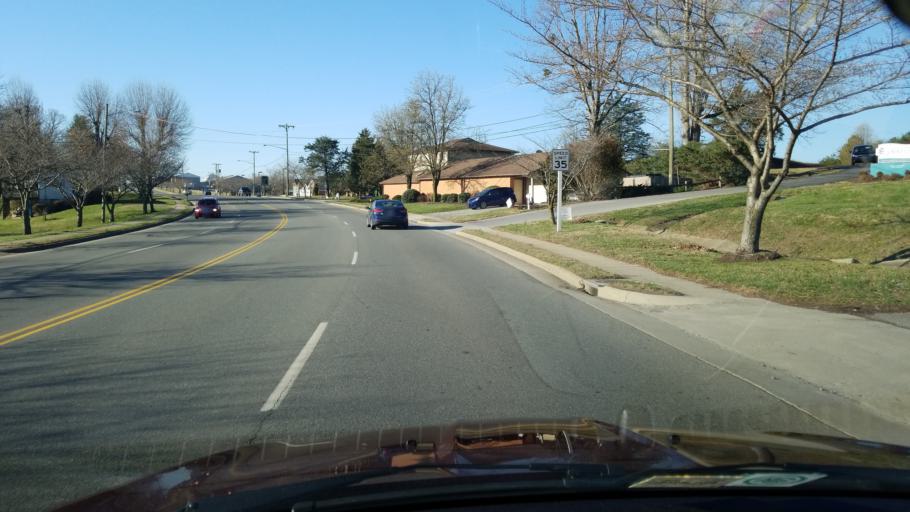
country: US
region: Virginia
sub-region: Franklin County
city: Rocky Mount
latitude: 37.0171
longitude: -79.8915
